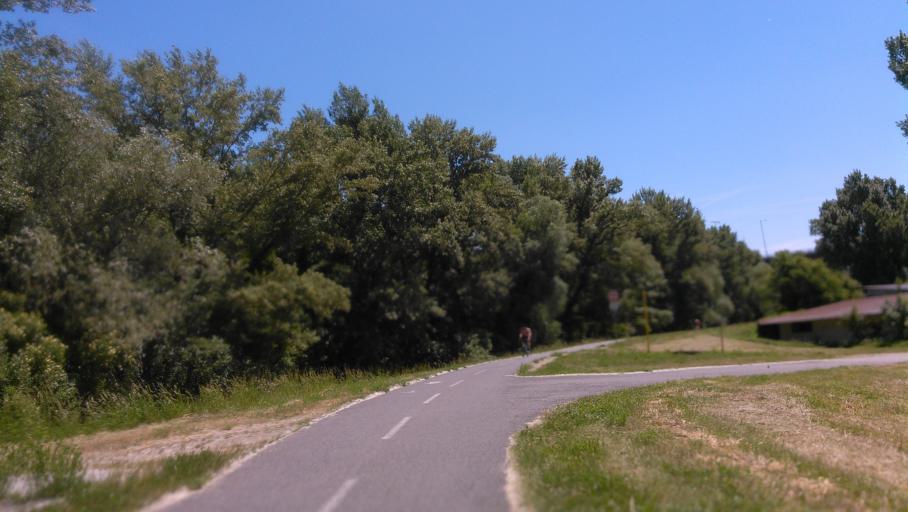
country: SK
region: Bratislavsky
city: Bratislava
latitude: 48.1332
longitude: 17.1323
